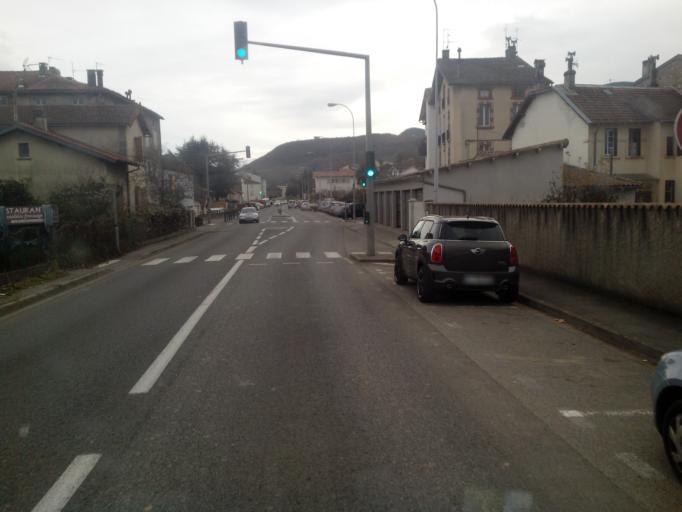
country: FR
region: Midi-Pyrenees
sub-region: Departement de l'Ariege
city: Saint-Girons
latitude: 42.9855
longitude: 1.1404
